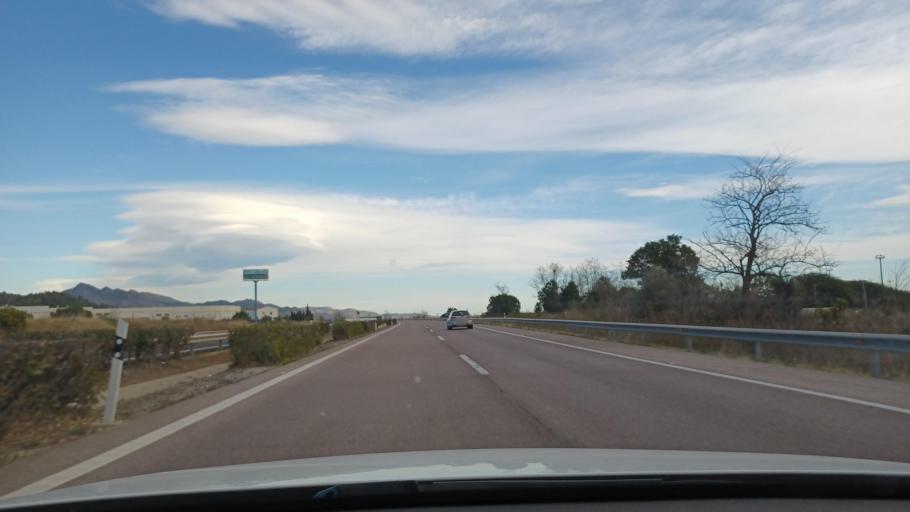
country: ES
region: Valencia
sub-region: Provincia de Castello
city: Castello de la Plana
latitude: 39.9971
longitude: -0.0751
